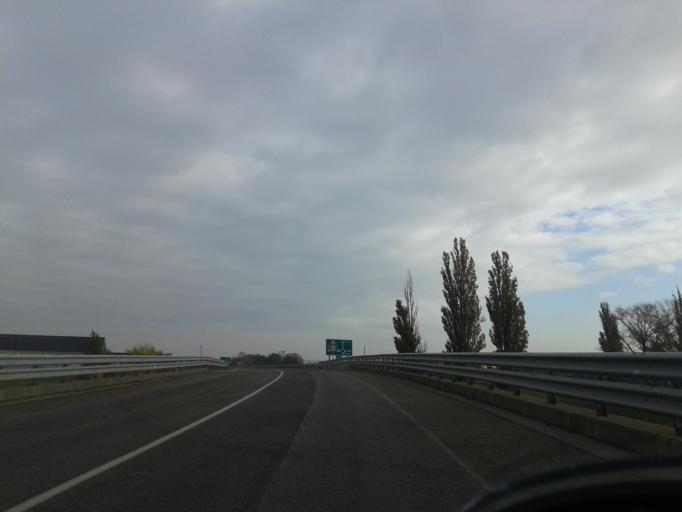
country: HU
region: Fejer
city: Ivancsa
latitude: 47.1299
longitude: 18.8184
